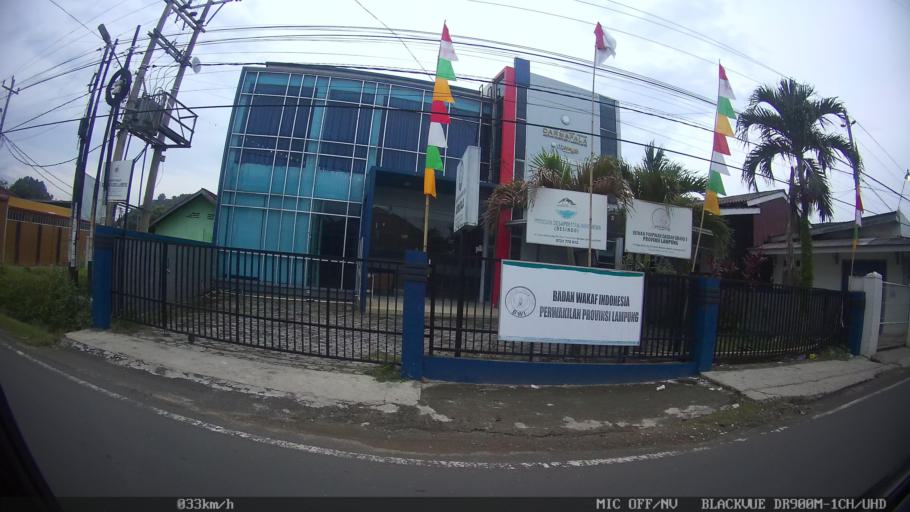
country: ID
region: Lampung
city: Kedaton
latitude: -5.3855
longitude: 105.2548
